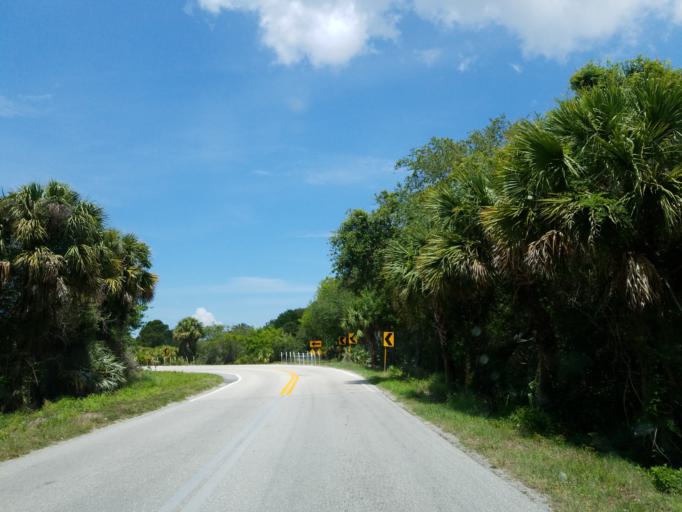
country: US
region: Florida
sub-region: Okeechobee County
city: Taylor Creek
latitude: 27.1623
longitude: -80.6754
